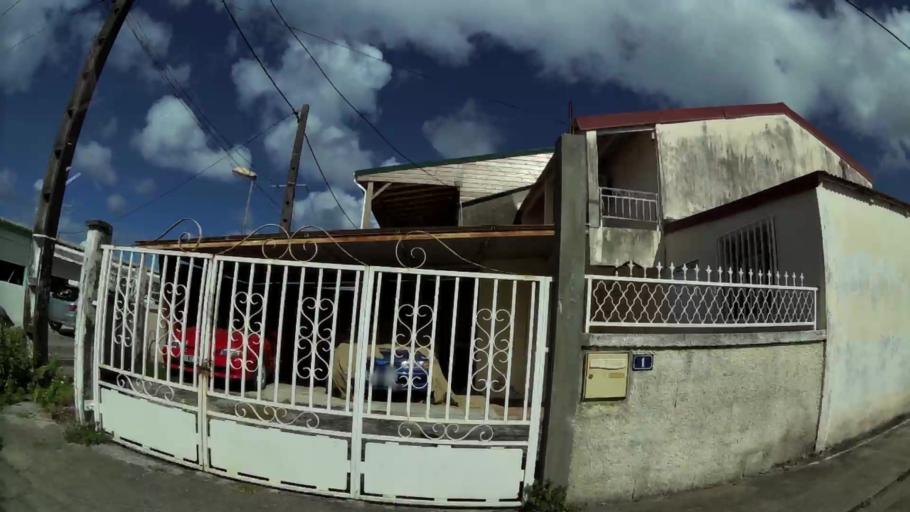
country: GP
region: Guadeloupe
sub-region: Guadeloupe
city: Port-Louis
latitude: 16.4213
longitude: -61.5318
